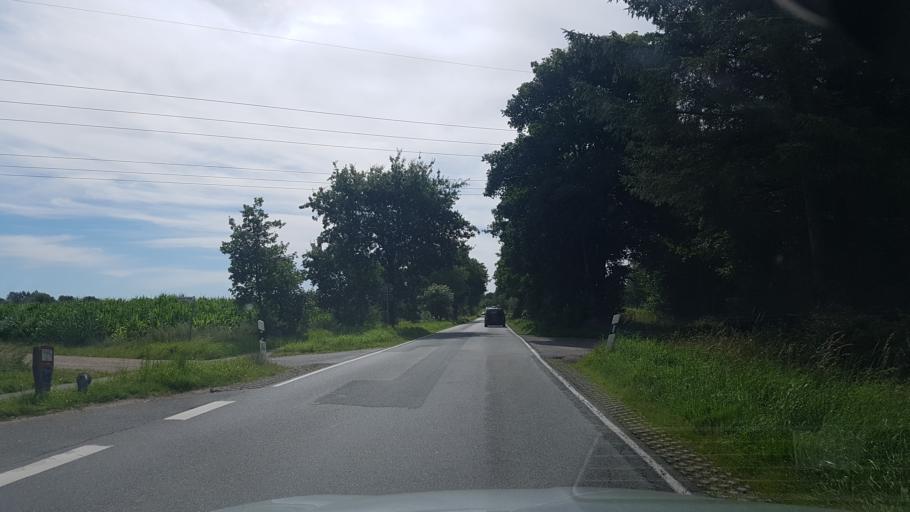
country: DE
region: Schleswig-Holstein
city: Handewitt
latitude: 54.7877
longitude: 9.3202
